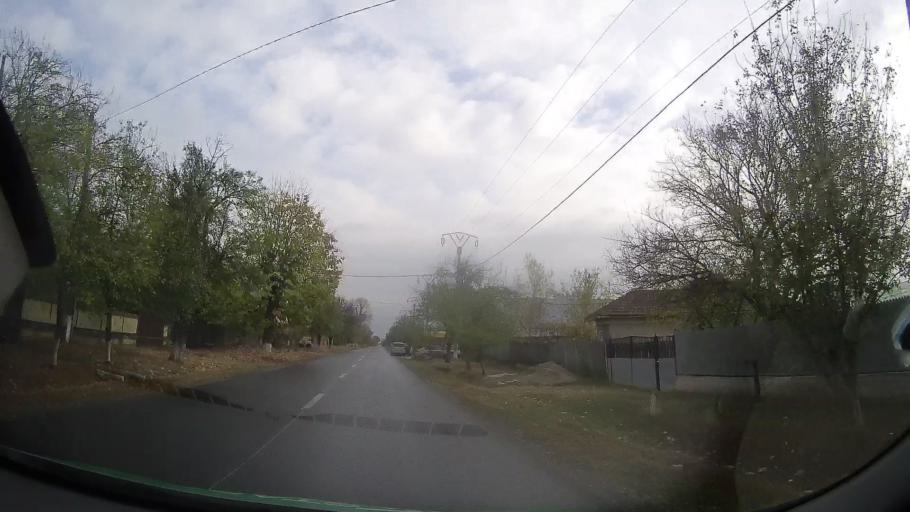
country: RO
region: Ialomita
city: Brazii
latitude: 44.7606
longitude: 26.3625
